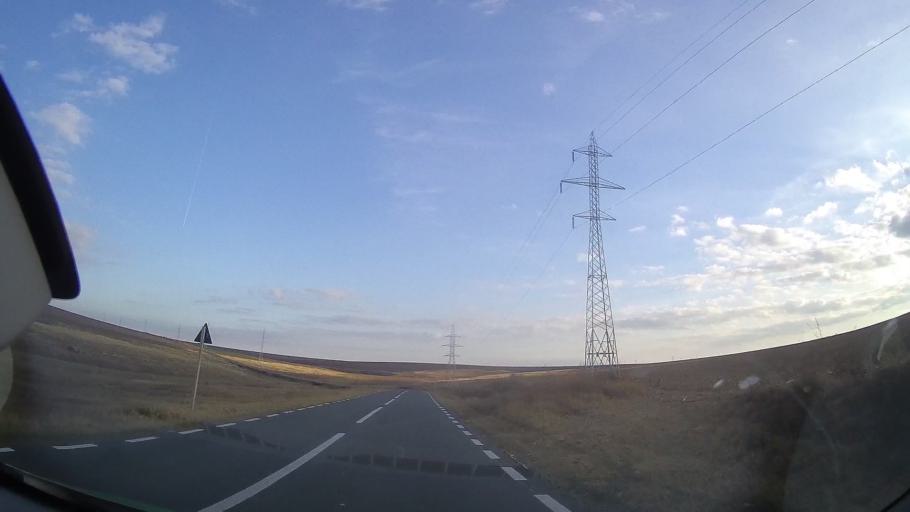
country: RO
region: Constanta
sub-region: Comuna Chirnogeni
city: Plopeni
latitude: 43.9557
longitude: 28.1498
